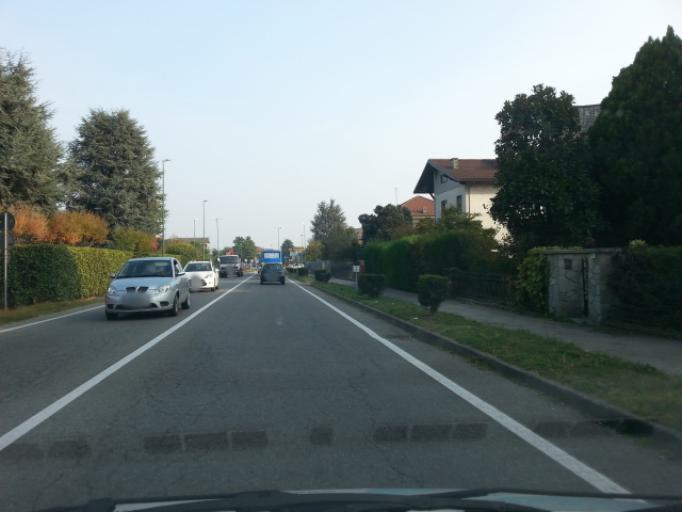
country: IT
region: Piedmont
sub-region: Provincia di Torino
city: Sangano
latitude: 45.0211
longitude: 7.4633
